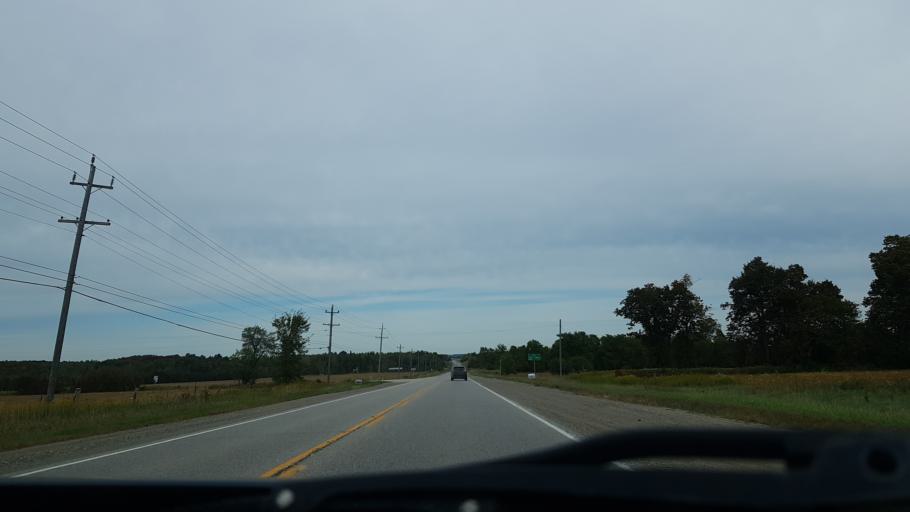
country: CA
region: Ontario
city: Orangeville
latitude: 43.7900
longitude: -80.0732
